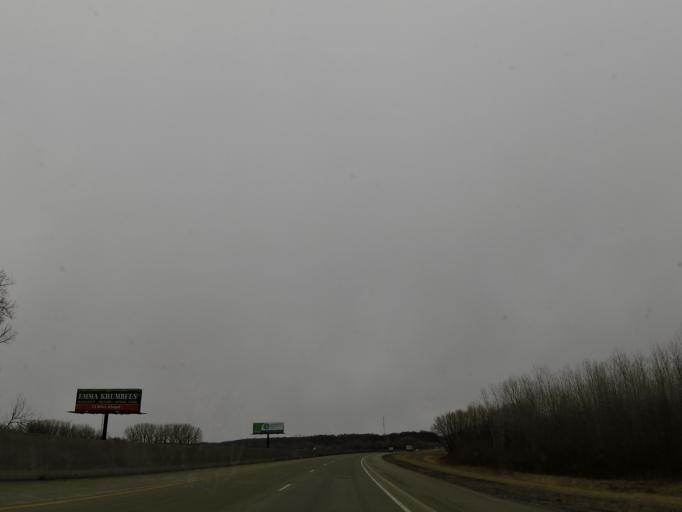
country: US
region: Minnesota
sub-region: Le Sueur County
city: Le Sueur
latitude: 44.4781
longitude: -93.9181
